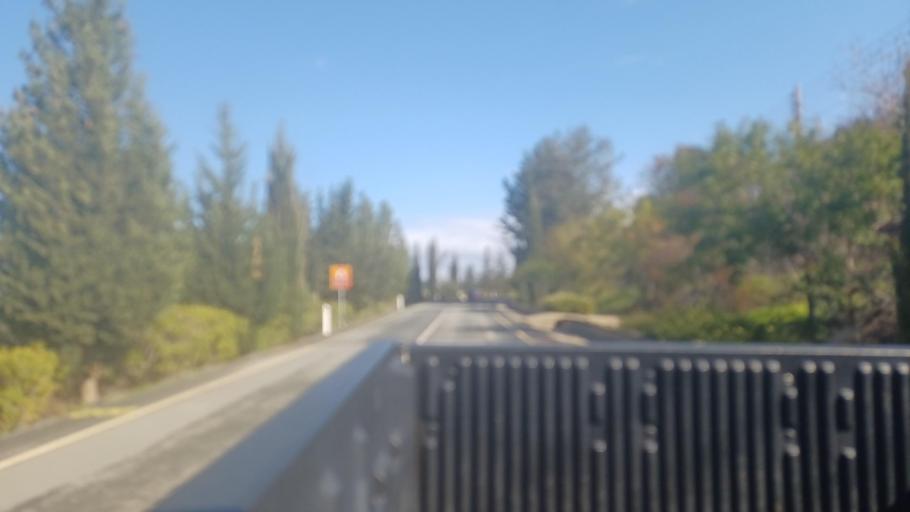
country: CY
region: Limassol
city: Pissouri
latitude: 34.7094
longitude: 32.5775
